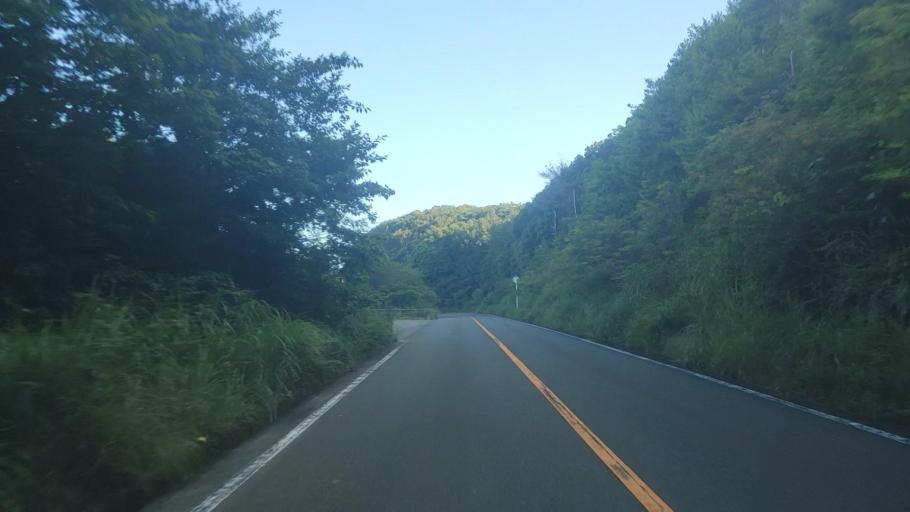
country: JP
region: Mie
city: Toba
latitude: 34.3894
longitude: 136.8619
